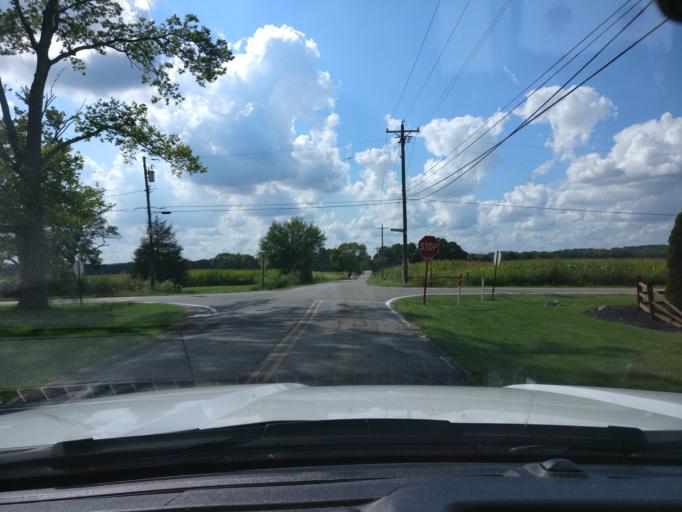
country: US
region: Ohio
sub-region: Warren County
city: Springboro
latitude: 39.5049
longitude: -84.2179
